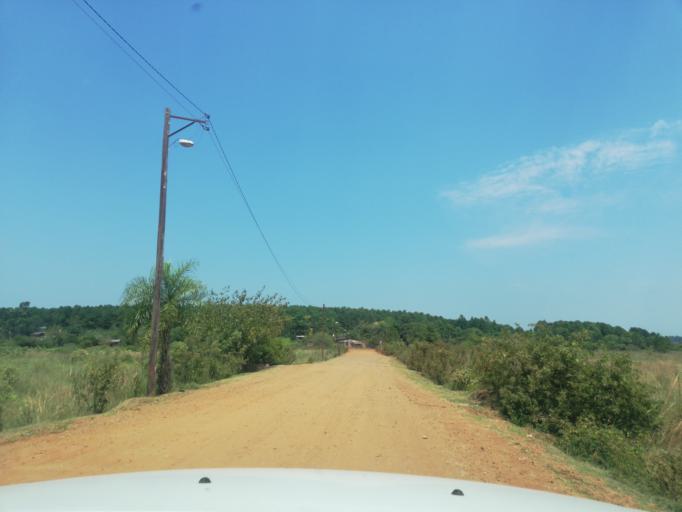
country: AR
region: Misiones
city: Garupa
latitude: -27.4495
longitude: -55.8929
